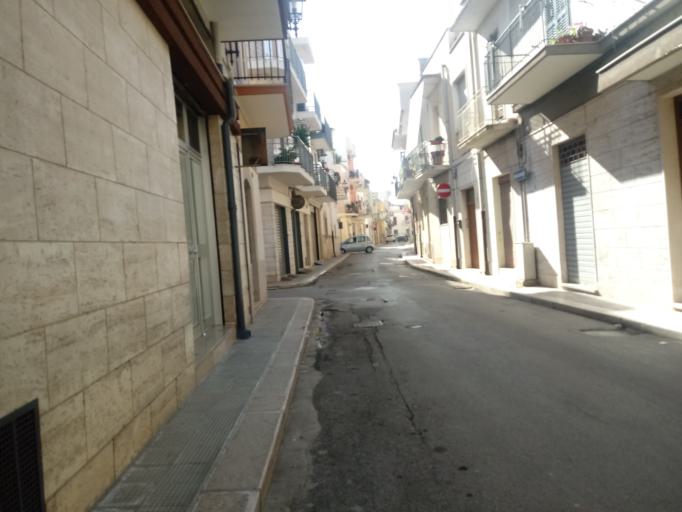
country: IT
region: Apulia
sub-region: Provincia di Barletta - Andria - Trani
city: Andria
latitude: 41.2229
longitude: 16.2967
